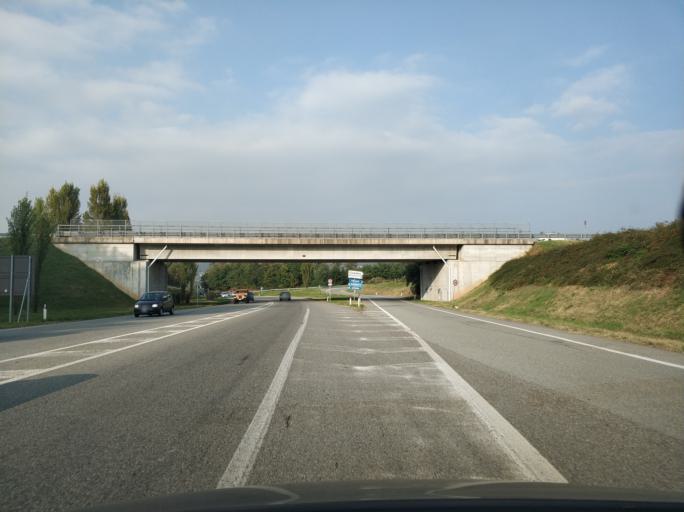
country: IT
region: Piedmont
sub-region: Provincia di Biella
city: Gaglianico
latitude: 45.5547
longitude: 8.0734
